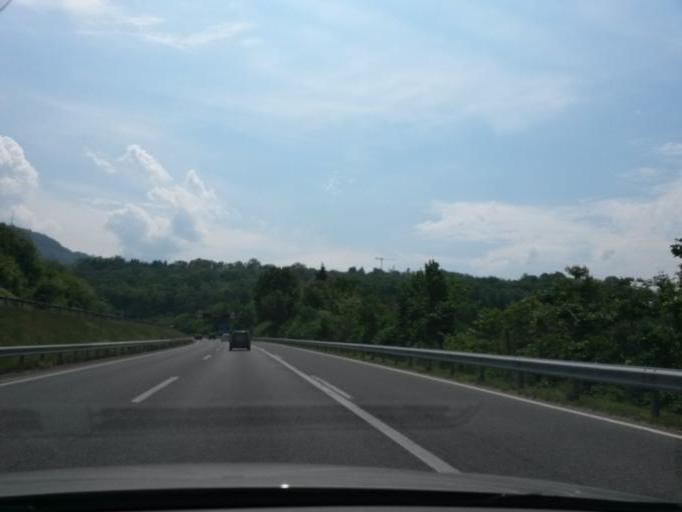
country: CH
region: Ticino
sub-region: Lugano District
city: Montagnola
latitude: 45.9953
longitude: 8.9176
